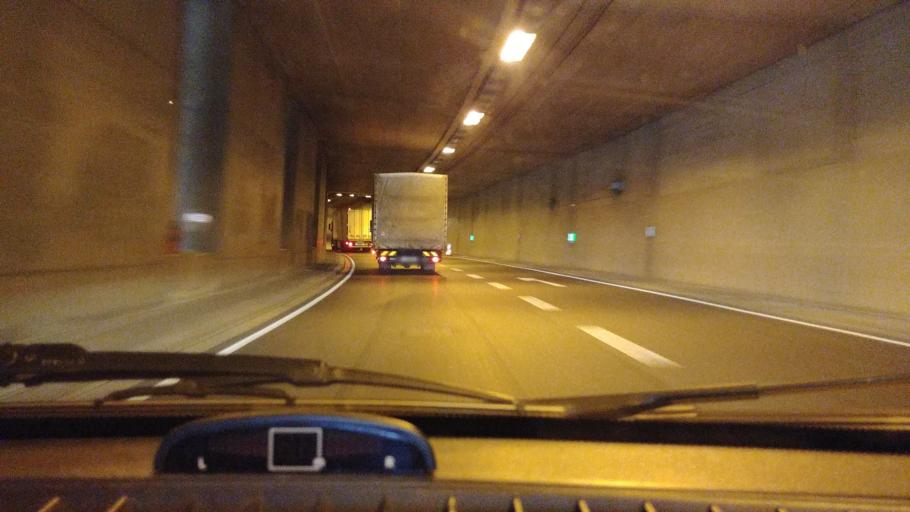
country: DE
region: Baden-Wuerttemberg
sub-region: Regierungsbezirk Stuttgart
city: Aalen
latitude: 48.8283
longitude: 10.0713
